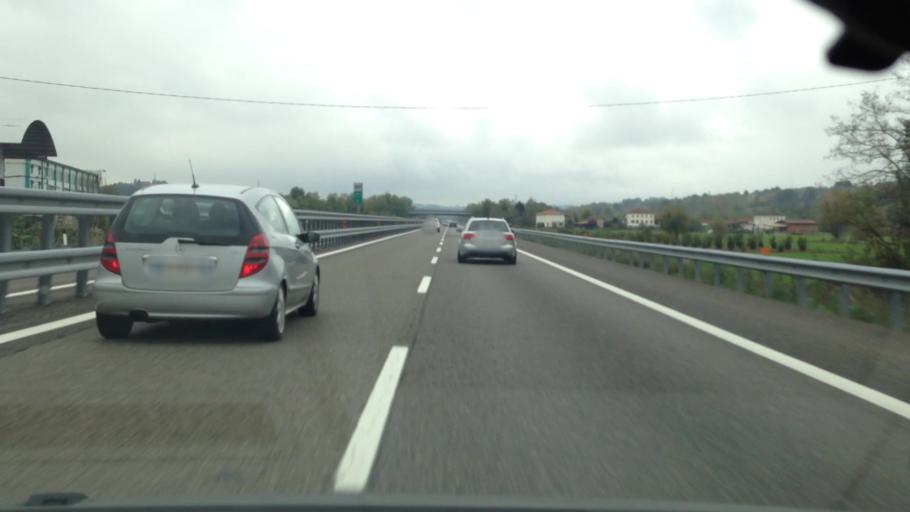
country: IT
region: Piedmont
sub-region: Provincia di Asti
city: Villafranca d'Asti
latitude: 44.9199
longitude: 8.0270
